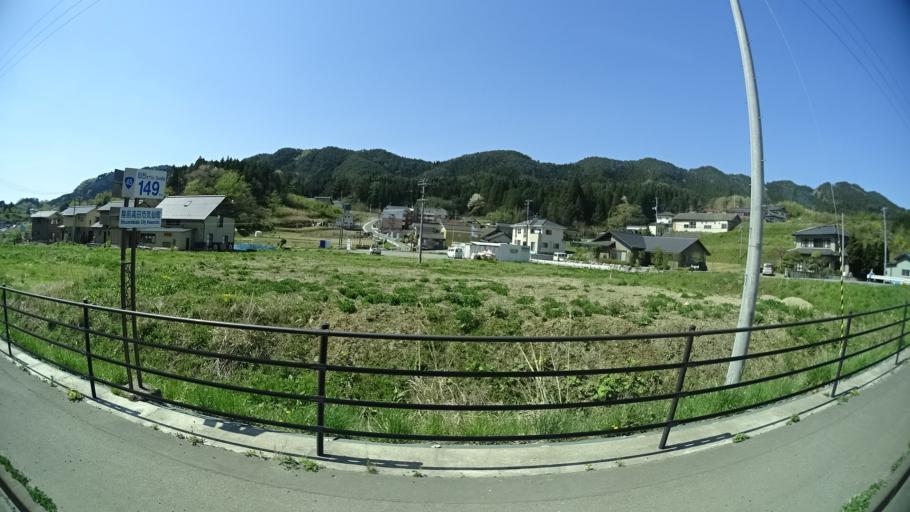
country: JP
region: Iwate
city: Ofunato
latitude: 38.9857
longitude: 141.6197
